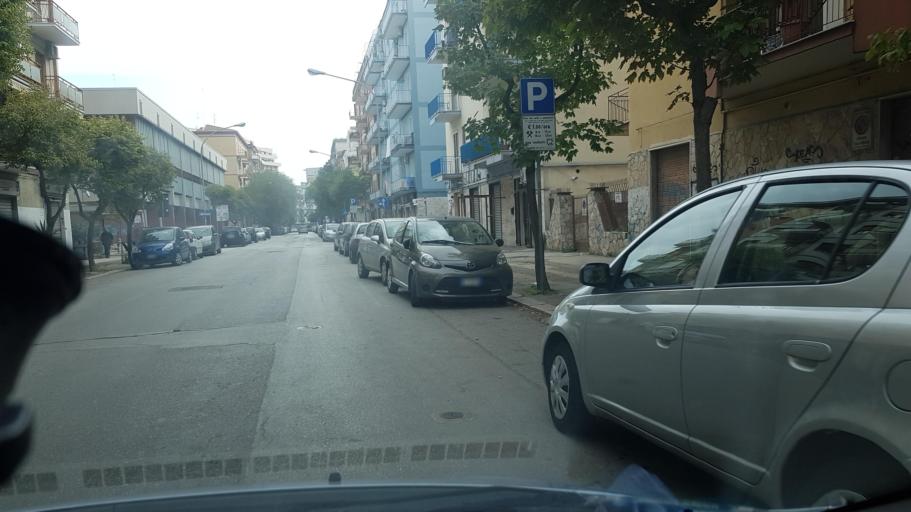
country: IT
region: Apulia
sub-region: Provincia di Foggia
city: Foggia
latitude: 41.4553
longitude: 15.5556
